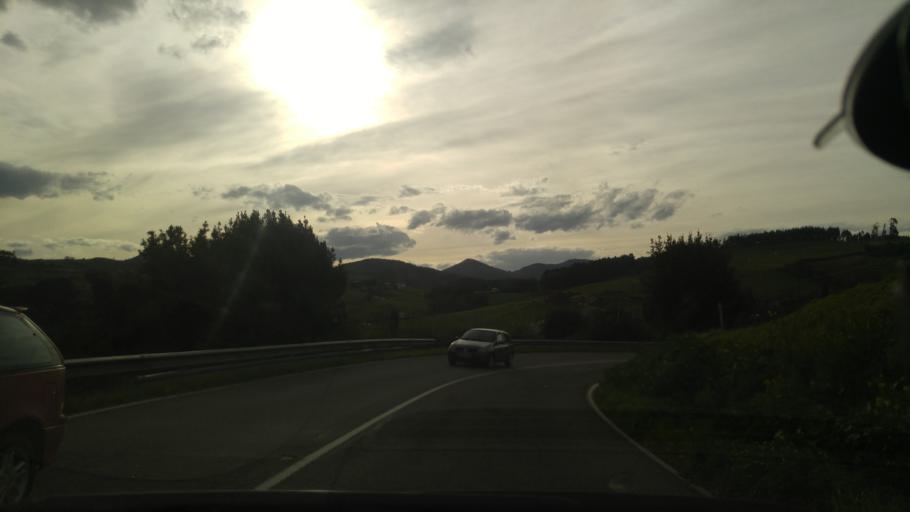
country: ES
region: Asturias
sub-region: Province of Asturias
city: Corvera de Asturias
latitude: 43.4812
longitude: -5.8491
